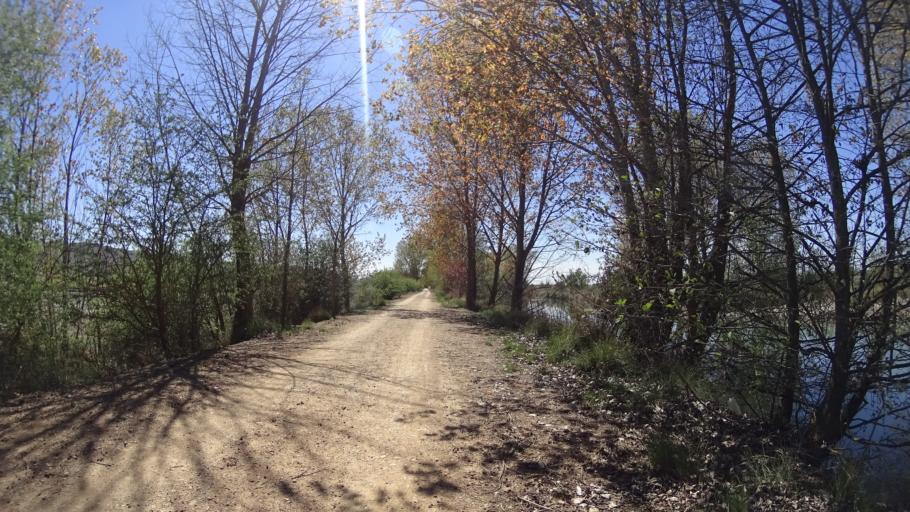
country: ES
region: Castille and Leon
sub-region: Provincia de Valladolid
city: Cabezon
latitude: 41.7722
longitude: -4.6184
